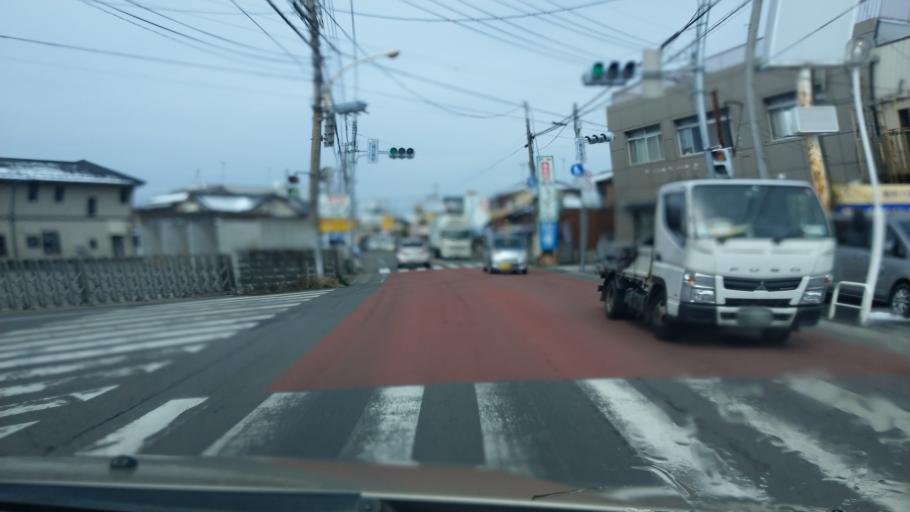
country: JP
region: Saitama
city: Yono
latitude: 35.9105
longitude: 139.5913
